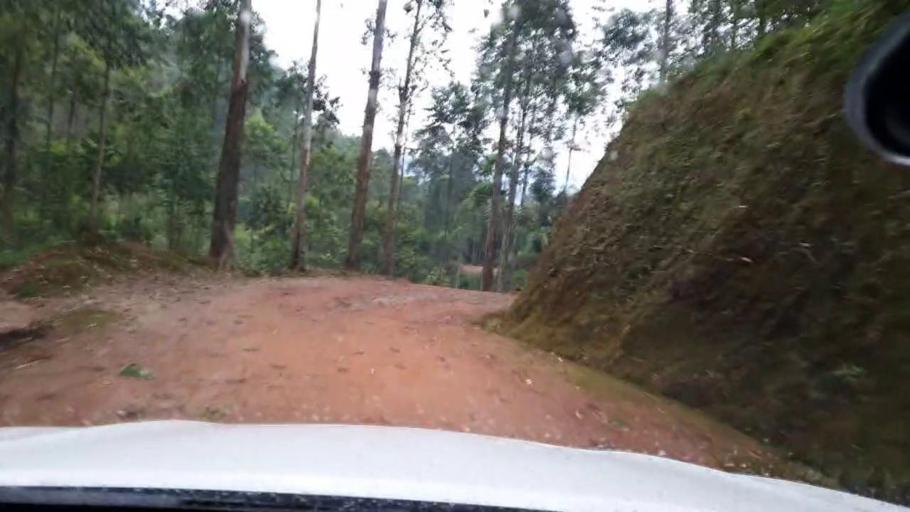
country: RW
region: Western Province
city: Cyangugu
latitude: -2.4088
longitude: 29.2028
